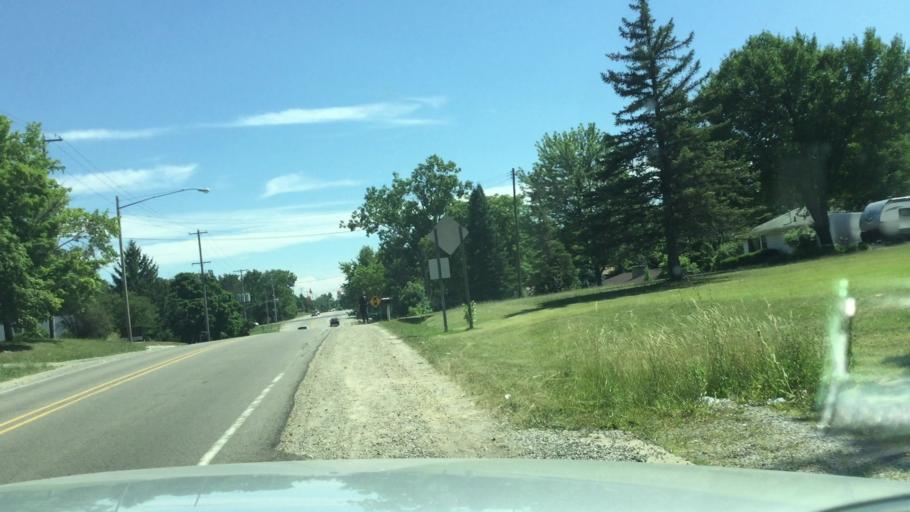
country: US
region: Michigan
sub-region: Genesee County
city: Flint
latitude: 43.0093
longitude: -83.7532
